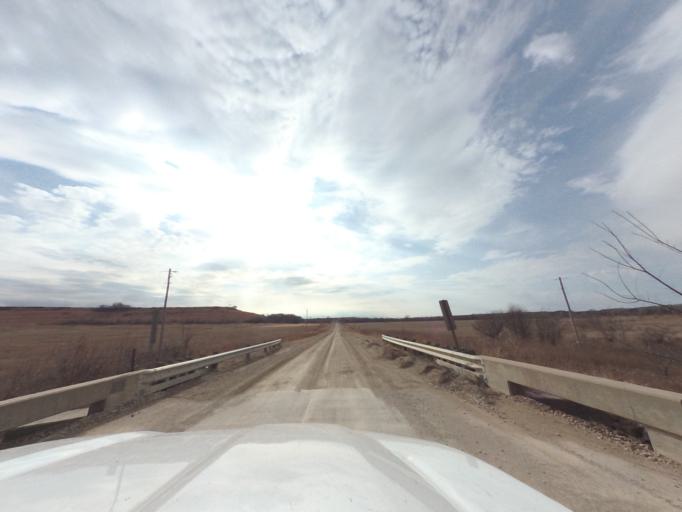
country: US
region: Kansas
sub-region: Chase County
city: Cottonwood Falls
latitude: 38.2946
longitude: -96.7321
